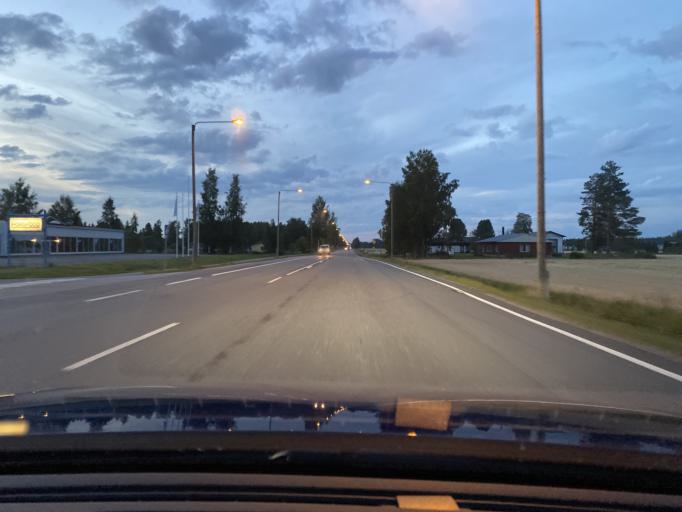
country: FI
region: Southern Ostrobothnia
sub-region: Suupohja
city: Kauhajoki
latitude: 62.4301
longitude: 22.2039
